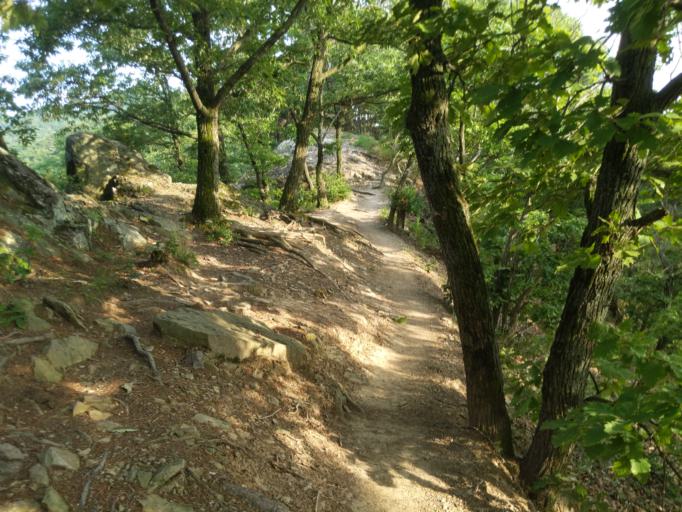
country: KR
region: Daegu
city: Hwawon
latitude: 35.7844
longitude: 128.5461
